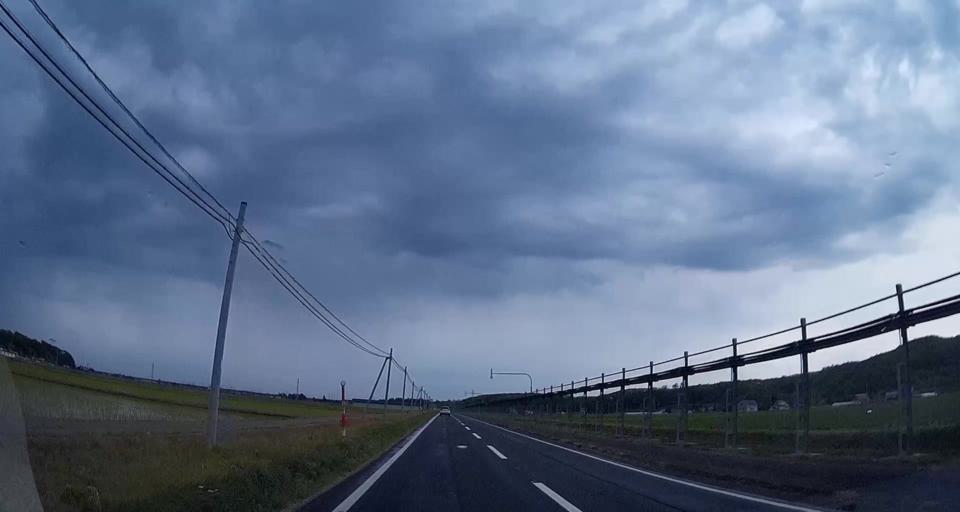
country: JP
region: Hokkaido
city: Chitose
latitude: 42.7164
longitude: 141.8639
